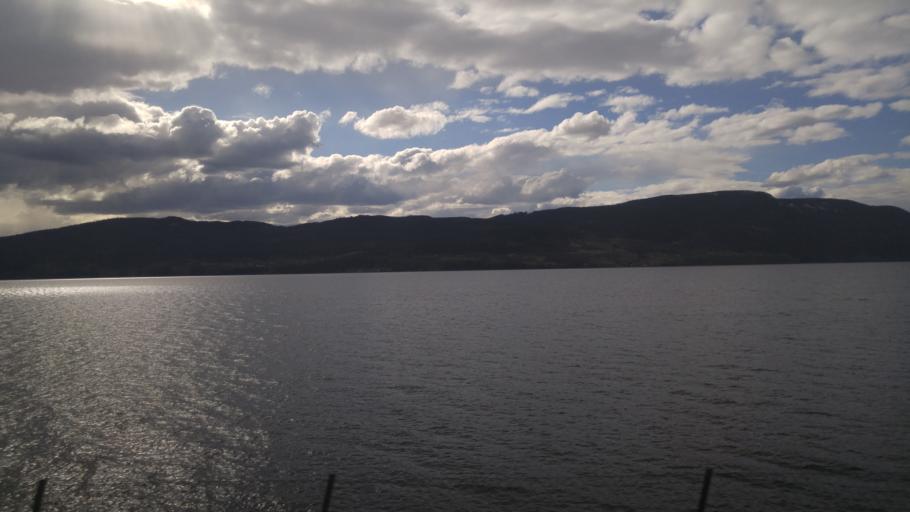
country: NO
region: Hedmark
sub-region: Stange
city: Stange
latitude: 60.5469
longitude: 11.2460
